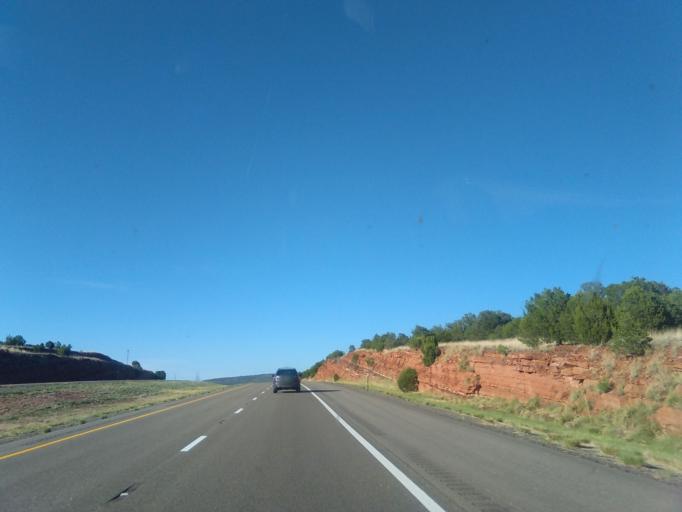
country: US
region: New Mexico
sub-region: San Miguel County
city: Las Vegas
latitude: 35.4443
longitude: -105.2830
